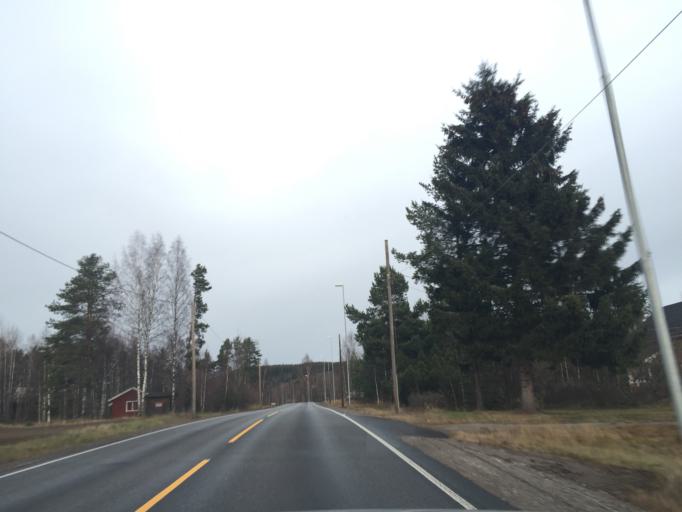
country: NO
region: Hedmark
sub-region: Asnes
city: Flisa
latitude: 60.5478
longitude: 12.0682
